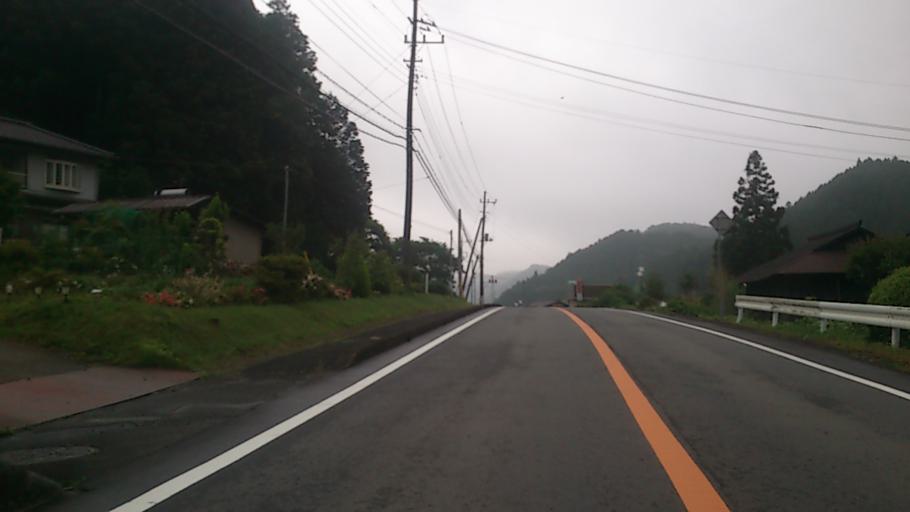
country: JP
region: Tochigi
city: Karasuyama
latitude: 36.6603
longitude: 140.2484
